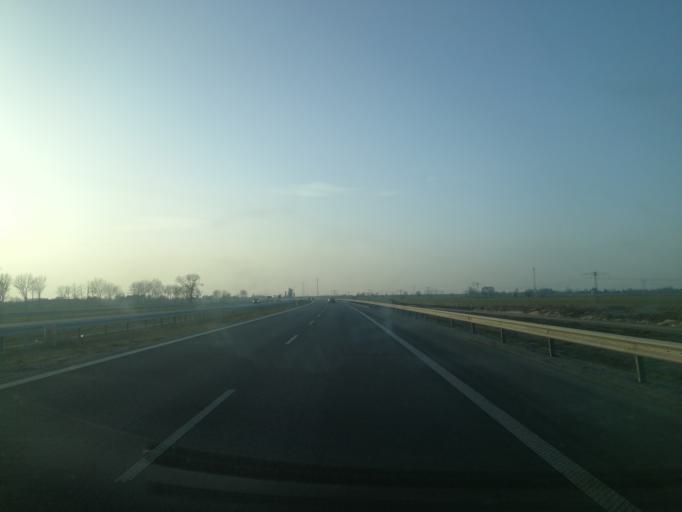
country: PL
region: Pomeranian Voivodeship
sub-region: Powiat nowodworski
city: Ostaszewo
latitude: 54.2522
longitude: 18.9790
